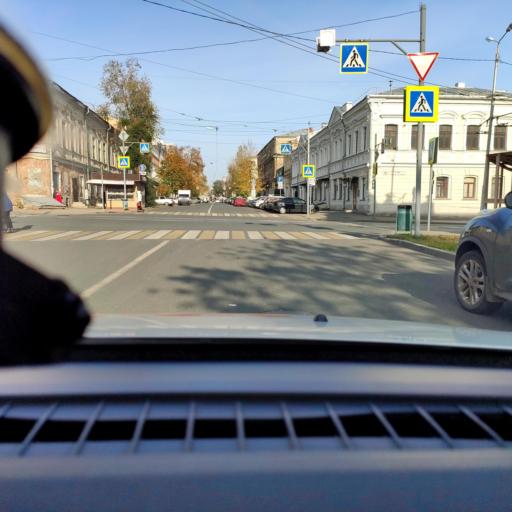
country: RU
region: Samara
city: Samara
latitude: 53.1837
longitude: 50.0941
